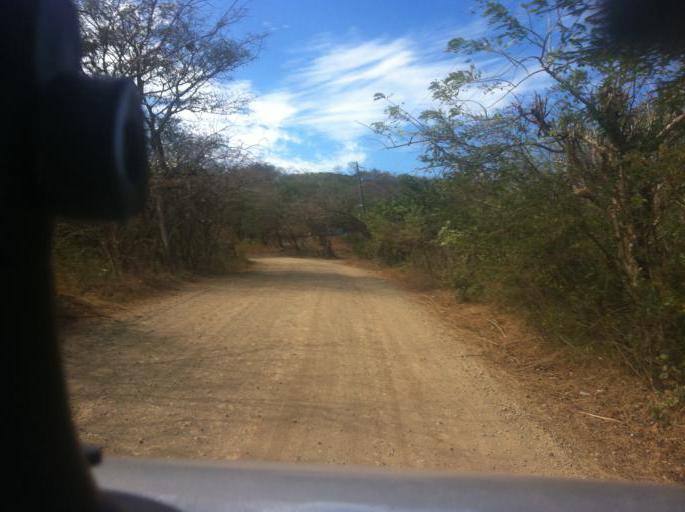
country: NI
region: Rivas
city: Tola
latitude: 11.4899
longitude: -86.0950
